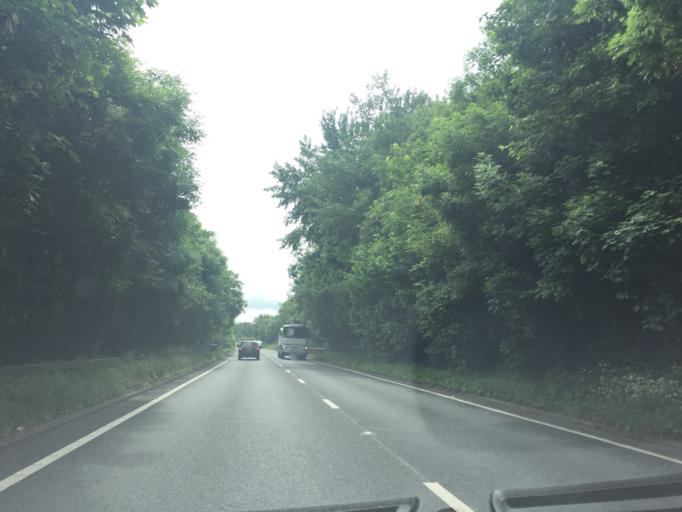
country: GB
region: England
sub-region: Dorset
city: Wimborne Minster
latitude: 50.7911
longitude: -1.9913
